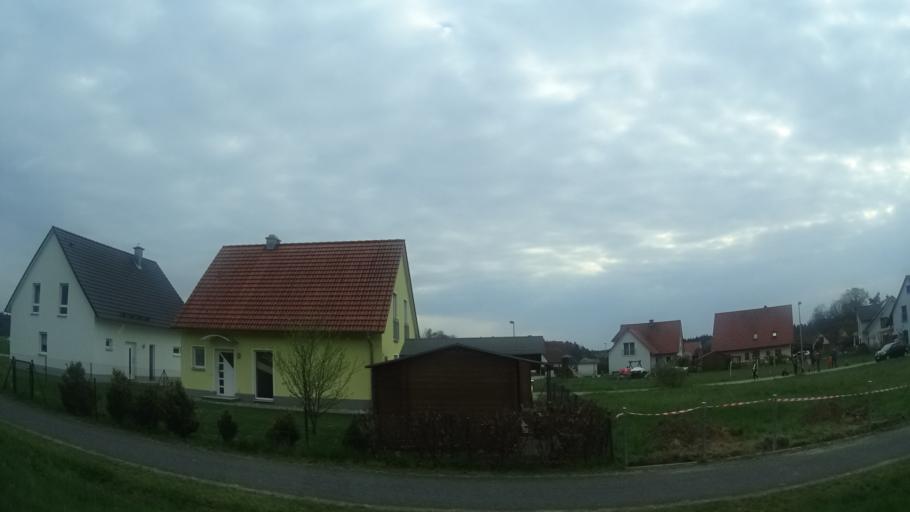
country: DE
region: Bavaria
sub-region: Regierungsbezirk Mittelfranken
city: Schnaittach
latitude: 49.5686
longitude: 11.3154
